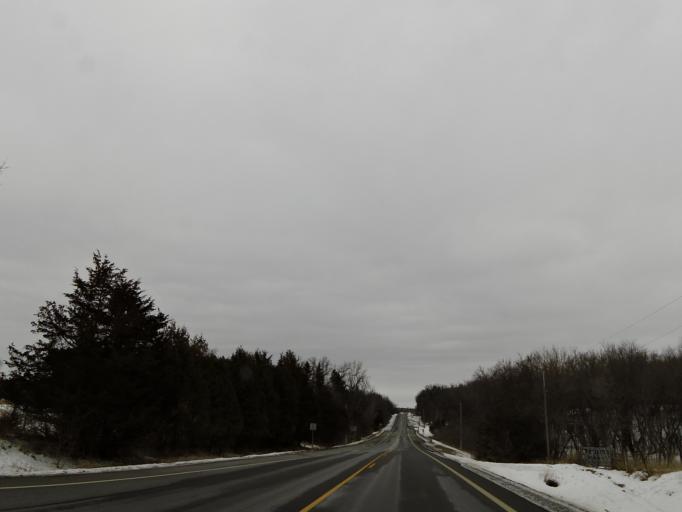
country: US
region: Wisconsin
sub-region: Pierce County
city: Prescott
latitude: 44.8017
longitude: -92.8063
